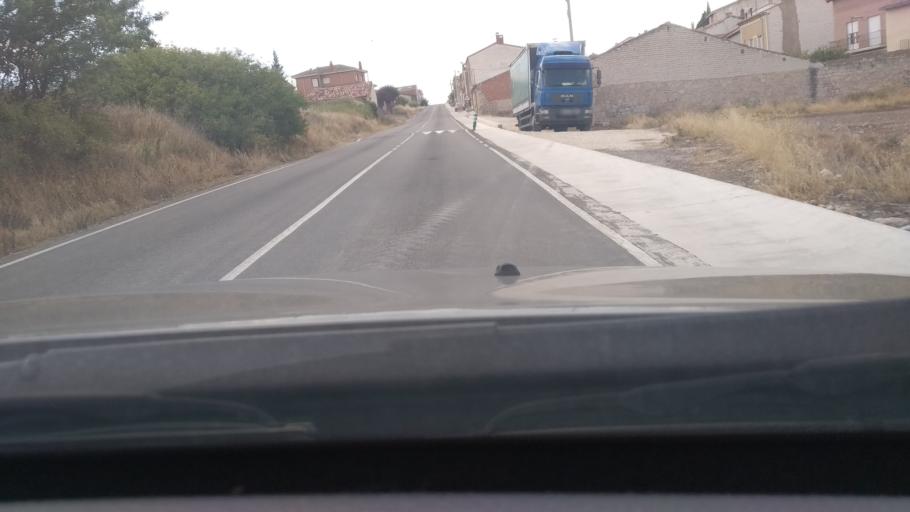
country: ES
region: Castille and Leon
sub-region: Provincia de Burgos
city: Villafruela
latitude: 41.9180
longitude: -3.9095
